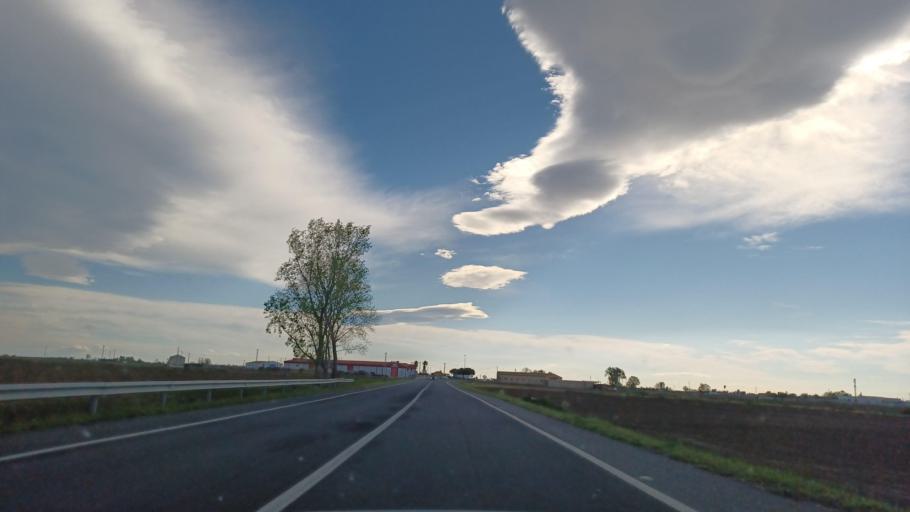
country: ES
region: Catalonia
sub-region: Provincia de Tarragona
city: Deltebre
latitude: 40.7286
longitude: 0.7049
